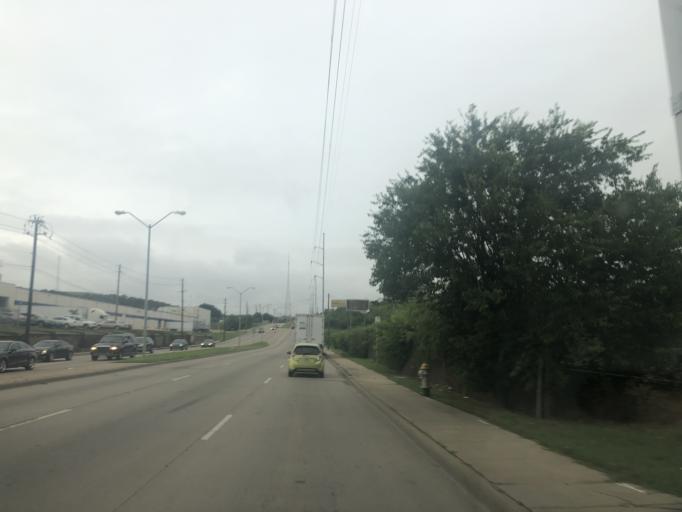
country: US
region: Texas
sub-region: Dallas County
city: Cockrell Hill
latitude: 32.7752
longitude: -96.8739
